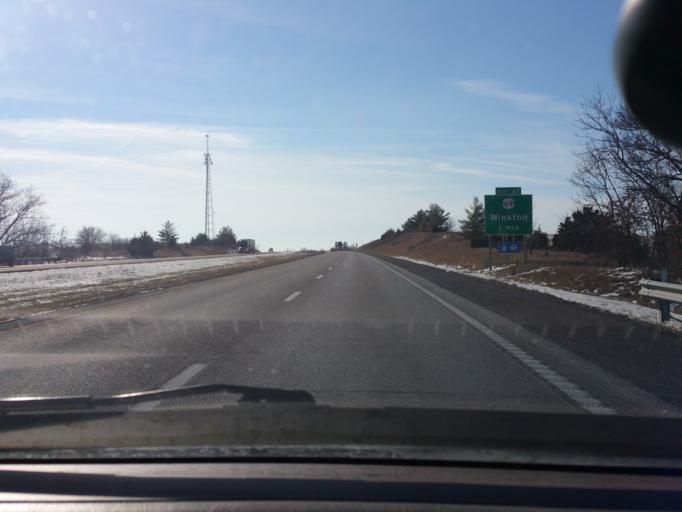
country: US
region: Missouri
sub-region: Clinton County
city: Cameron
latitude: 39.8739
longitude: -94.1674
